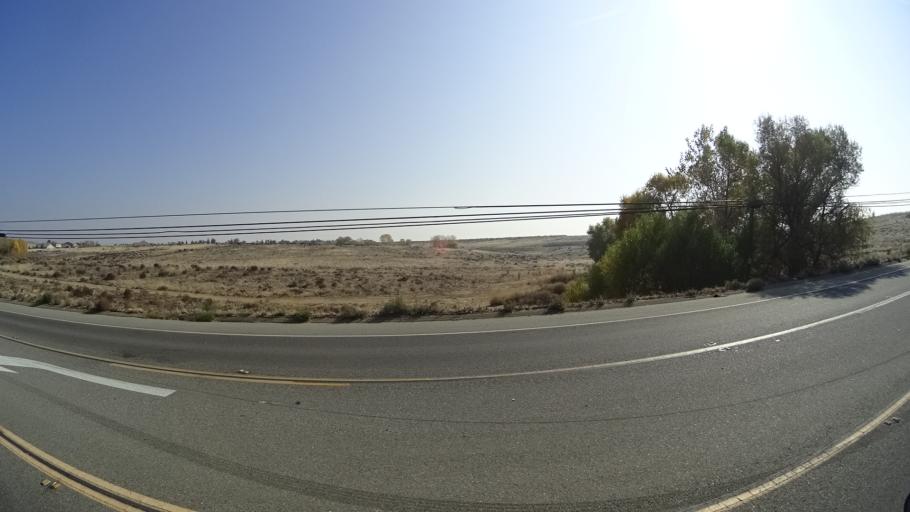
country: US
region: California
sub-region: Kern County
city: Bakersfield
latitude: 35.3905
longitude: -118.8891
